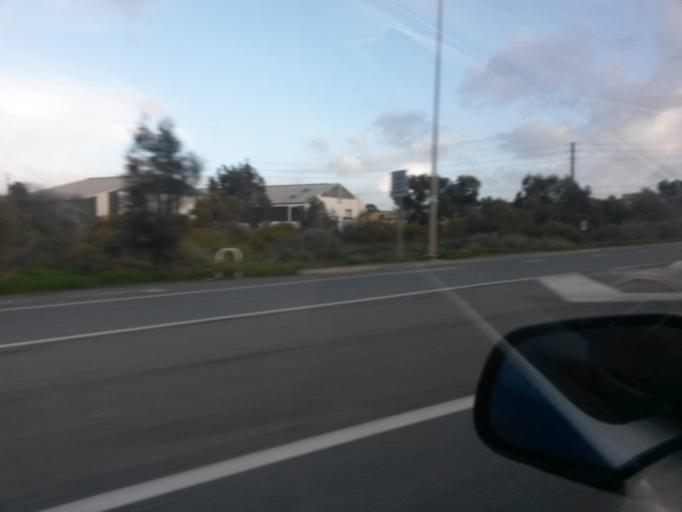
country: AU
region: South Australia
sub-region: Port Adelaide Enfield
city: Alberton
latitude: -34.8376
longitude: 138.5243
